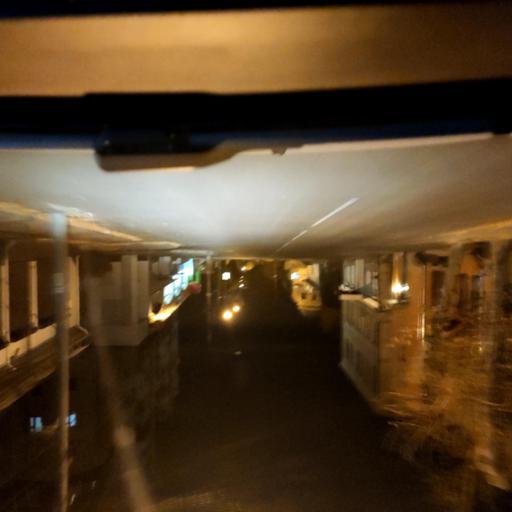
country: RU
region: Voronezj
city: Voronezh
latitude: 51.6810
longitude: 39.2204
